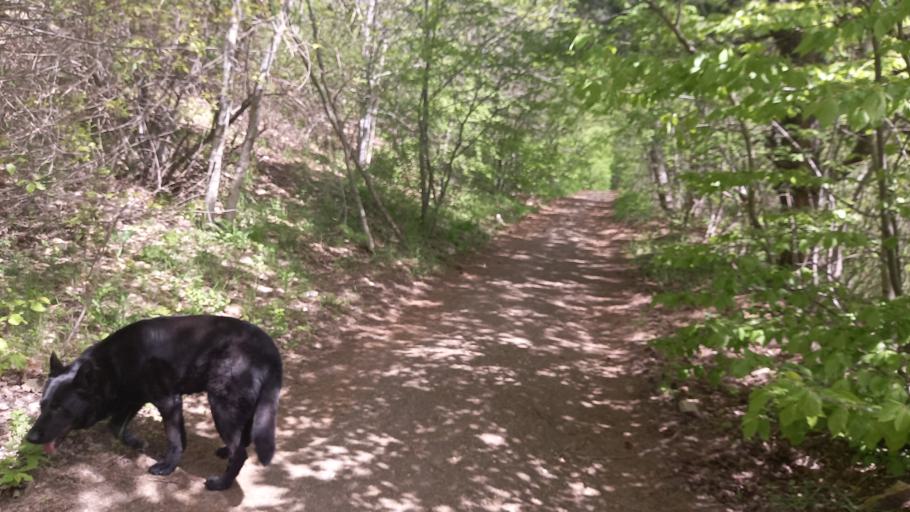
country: RU
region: Stavropol'skiy
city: Pyatigorsk
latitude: 44.0881
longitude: 43.0294
